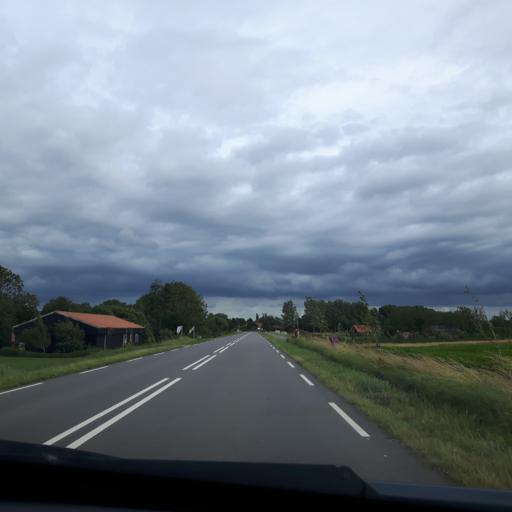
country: NL
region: Zeeland
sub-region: Gemeente Noord-Beveland
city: Kamperland
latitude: 51.5666
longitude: 3.7935
